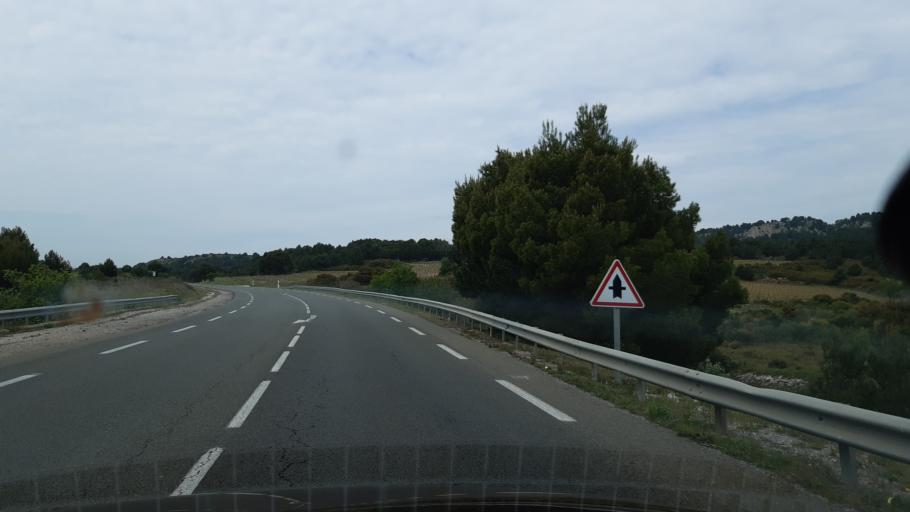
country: FR
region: Languedoc-Roussillon
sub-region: Departement de l'Aude
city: Gruissan
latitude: 43.1223
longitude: 3.0749
